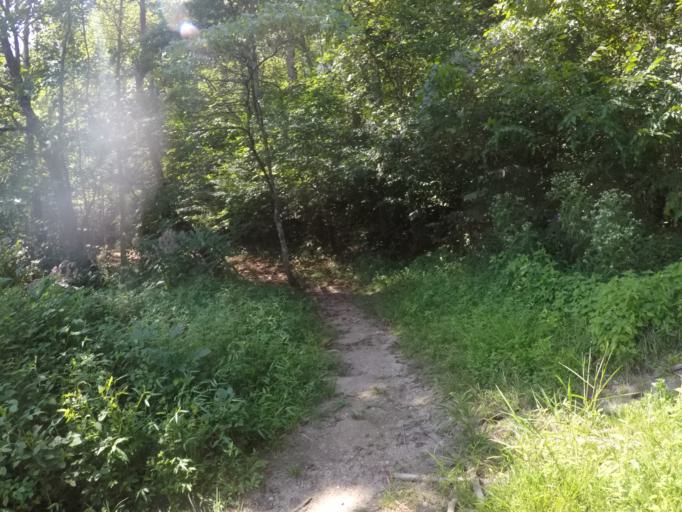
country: US
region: Ohio
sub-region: Lawrence County
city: Ironton
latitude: 38.6121
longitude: -82.6290
